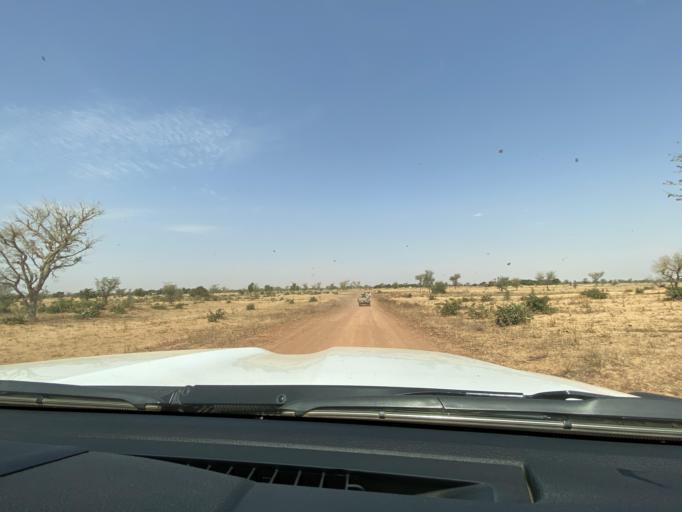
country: NE
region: Dosso
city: Birnin Gaoure
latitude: 13.2343
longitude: 2.8683
